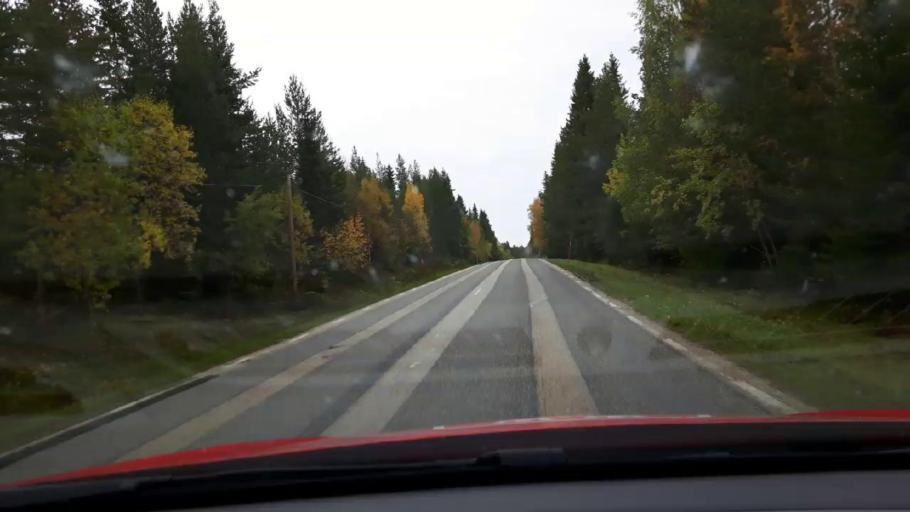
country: SE
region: Jaemtland
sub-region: Bergs Kommun
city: Hoverberg
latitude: 62.8982
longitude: 14.3458
